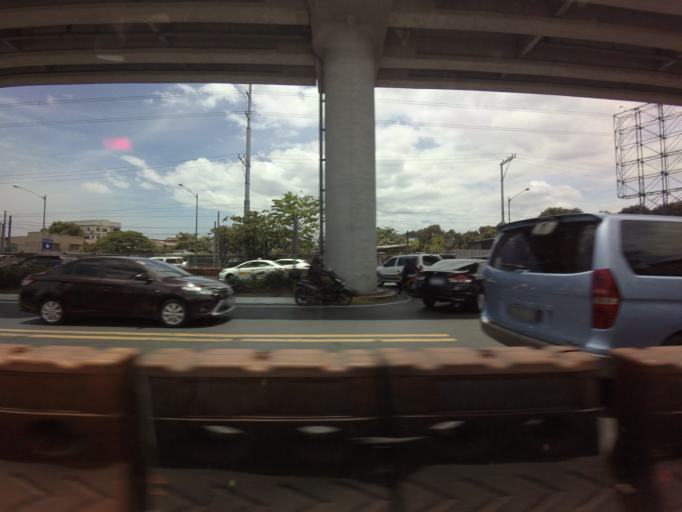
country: PH
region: Metro Manila
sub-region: Marikina
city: Calumpang
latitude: 14.6212
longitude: 121.1048
